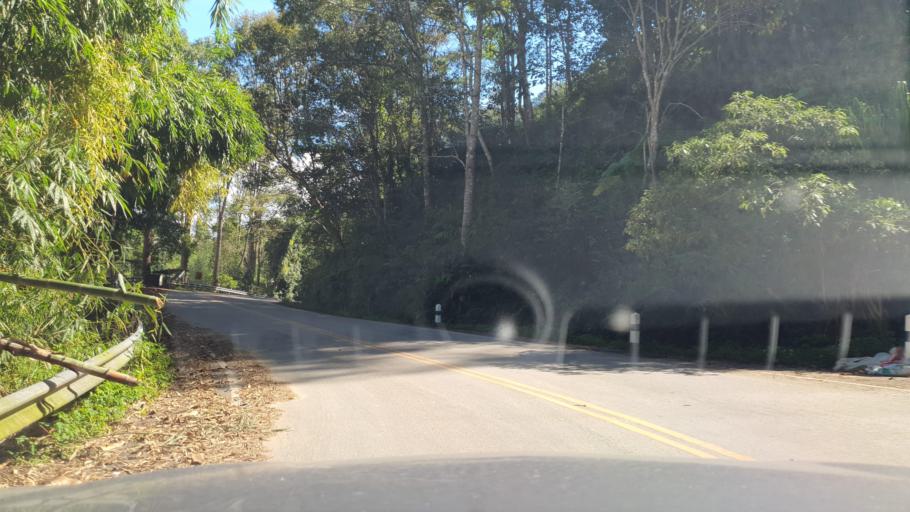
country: TH
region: Chiang Mai
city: Phrao
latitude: 19.3160
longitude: 99.3290
